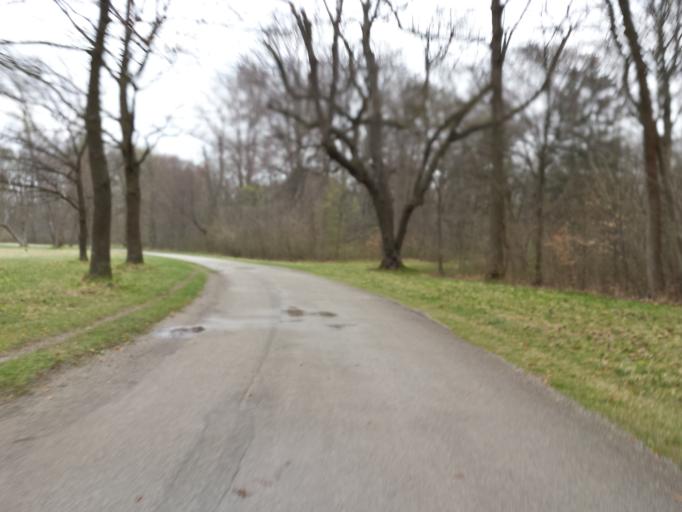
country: DE
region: Bavaria
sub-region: Upper Bavaria
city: Unterfoehring
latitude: 48.1813
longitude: 11.6203
